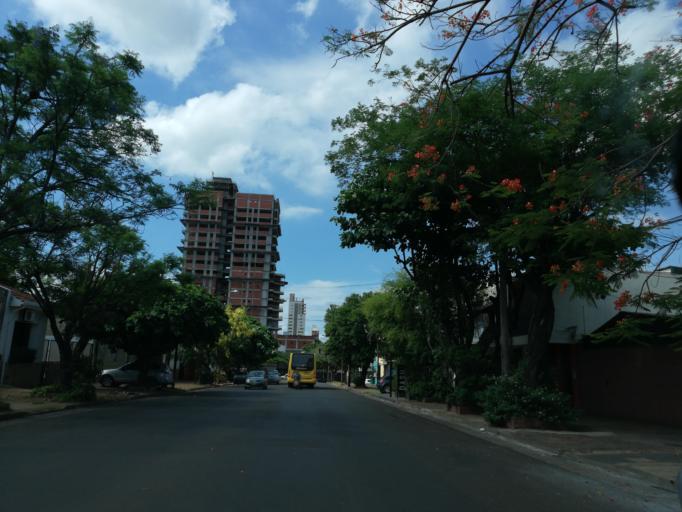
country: AR
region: Misiones
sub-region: Departamento de Capital
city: Posadas
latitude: -27.3762
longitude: -55.8912
